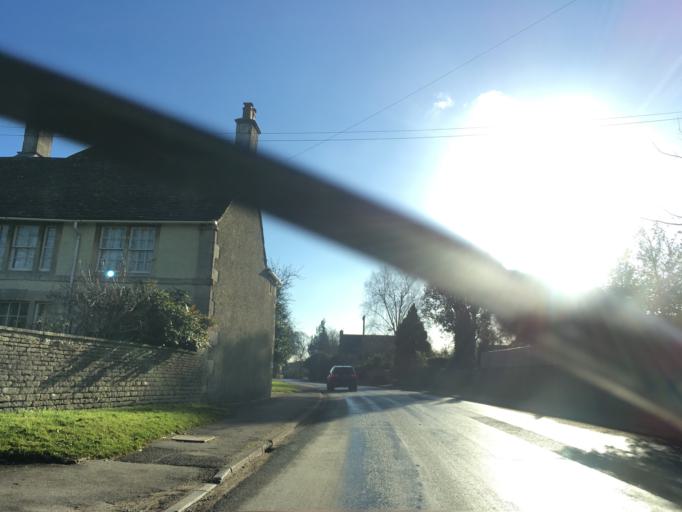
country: GB
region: England
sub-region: Wiltshire
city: Biddestone
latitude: 51.4860
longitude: -2.1932
